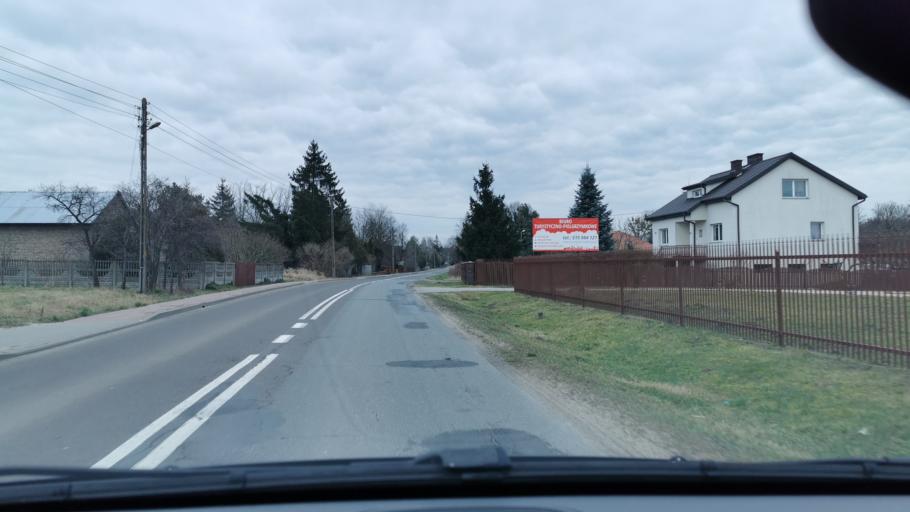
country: PL
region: Masovian Voivodeship
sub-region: Powiat zyrardowski
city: Radziejowice
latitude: 52.0082
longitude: 20.5469
